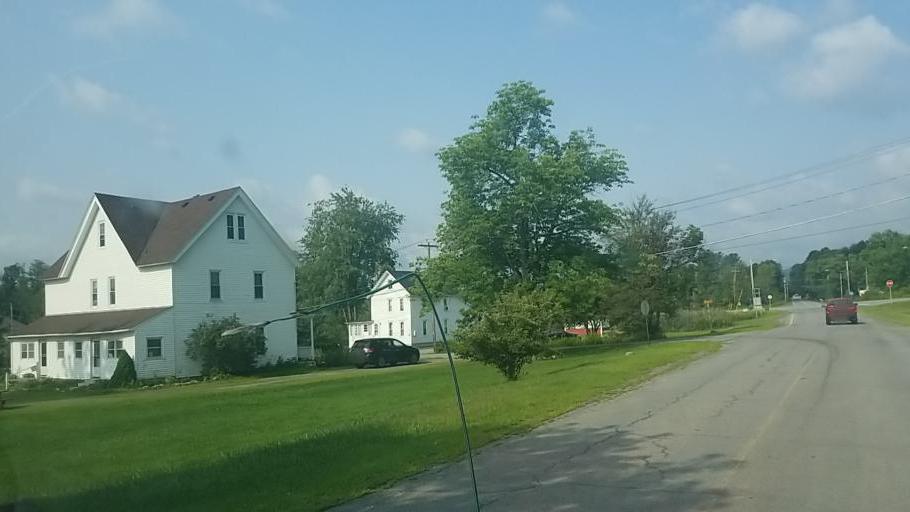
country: US
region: New York
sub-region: Fulton County
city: Broadalbin
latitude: 43.1045
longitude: -74.2712
